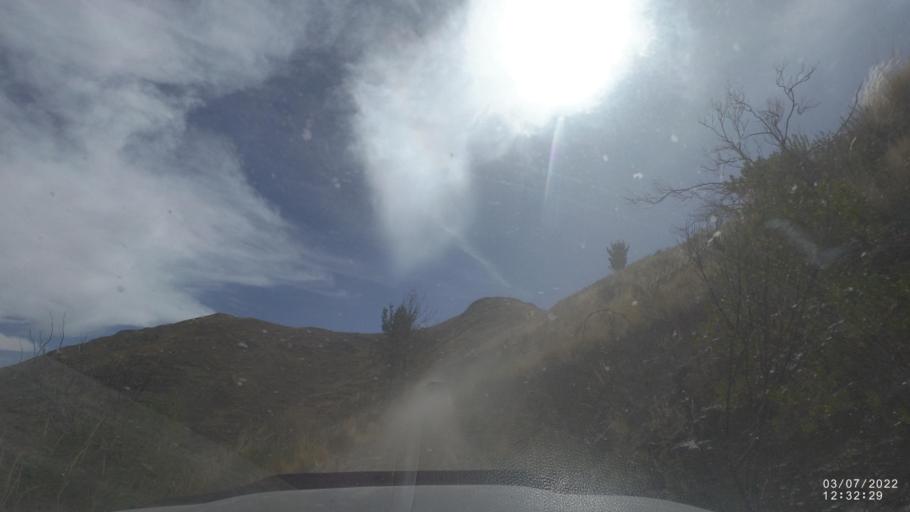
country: BO
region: Cochabamba
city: Irpa Irpa
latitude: -17.8094
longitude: -66.6057
